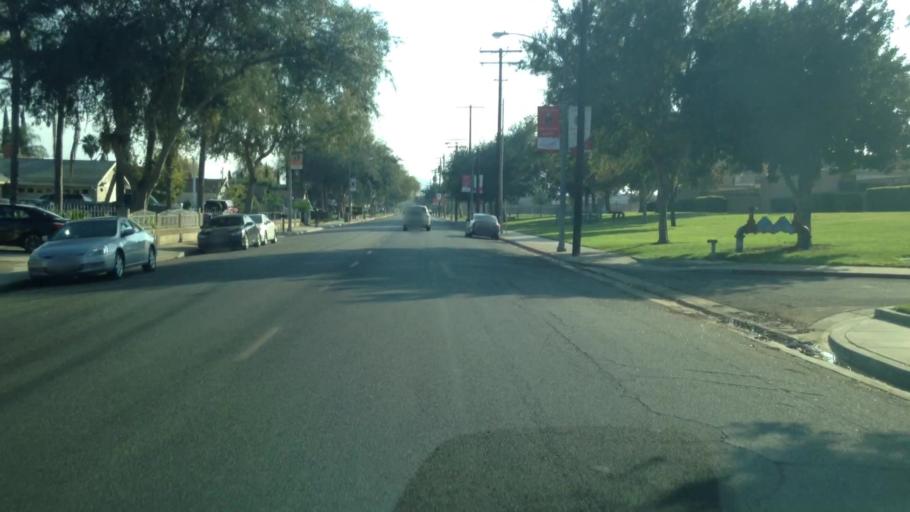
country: US
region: California
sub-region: Riverside County
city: Pedley
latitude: 33.9500
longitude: -117.4726
